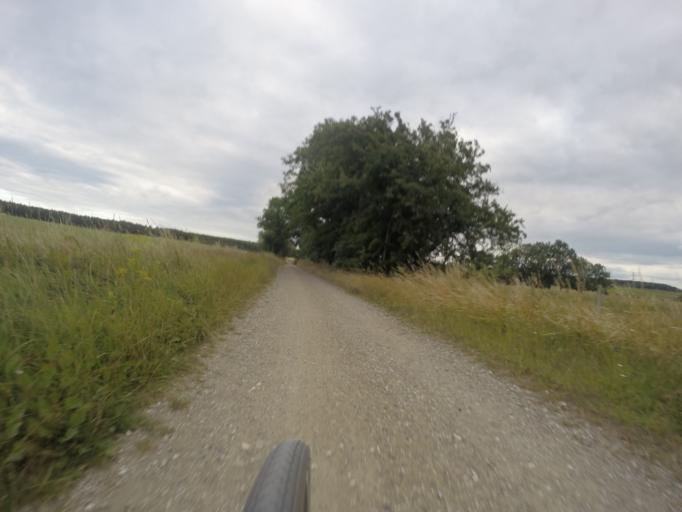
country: DK
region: Capital Region
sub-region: Hoje-Taastrup Kommune
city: Taastrup
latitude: 55.6940
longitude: 12.3165
